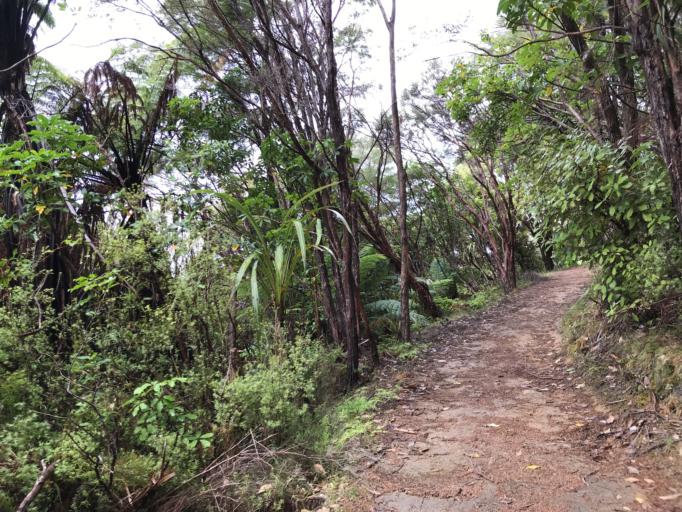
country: NZ
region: Marlborough
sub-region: Marlborough District
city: Picton
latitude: -41.1138
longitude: 174.1641
